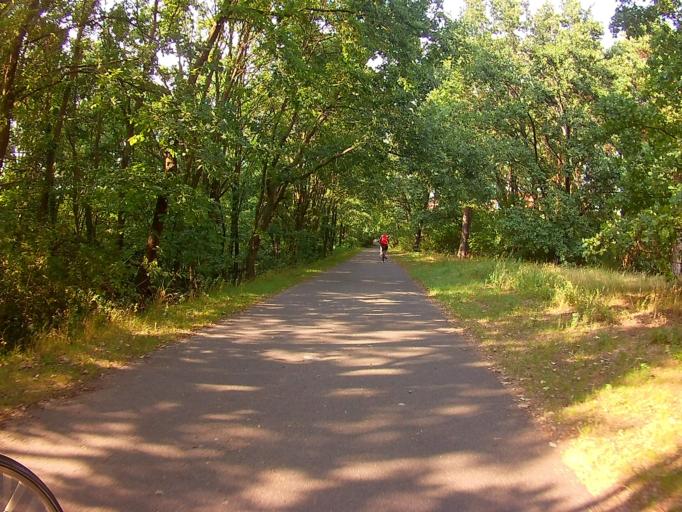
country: DE
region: Berlin
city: Kopenick Bezirk
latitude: 52.4701
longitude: 13.5671
